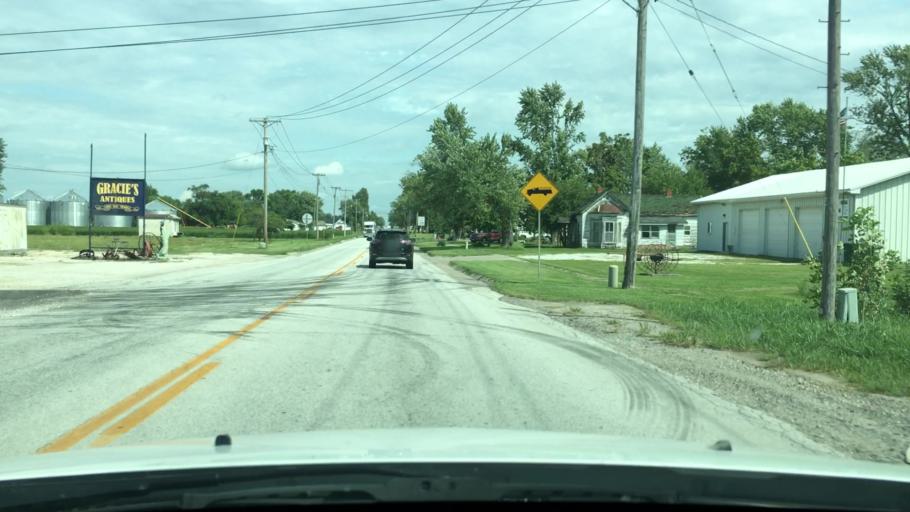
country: US
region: Missouri
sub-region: Audrain County
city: Vandalia
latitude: 39.2431
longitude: -91.6455
